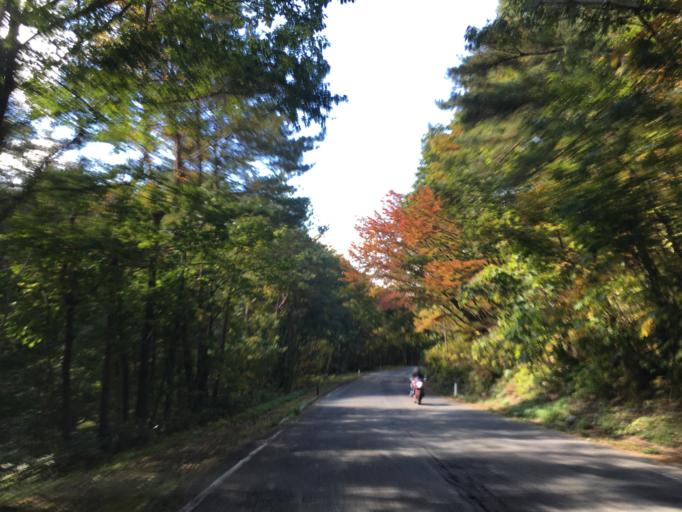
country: JP
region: Fukushima
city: Inawashiro
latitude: 37.6126
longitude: 140.2160
